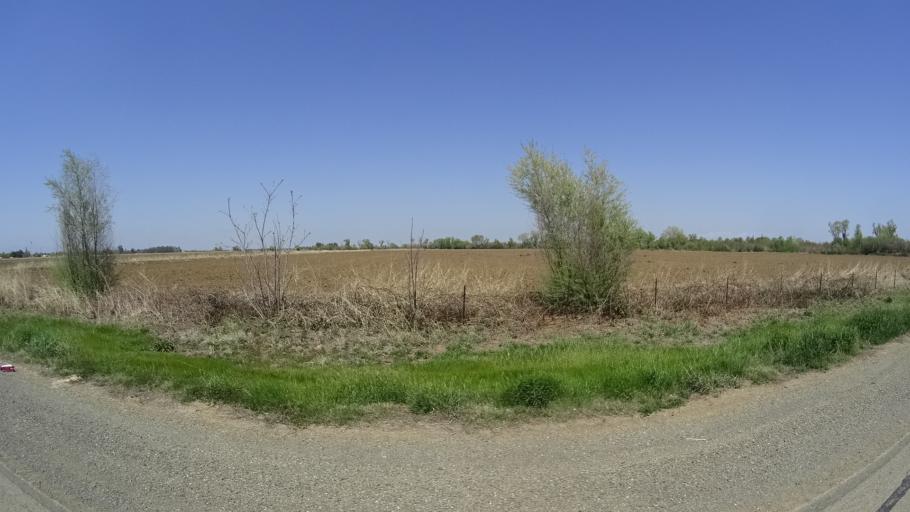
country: US
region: California
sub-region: Glenn County
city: Willows
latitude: 39.5242
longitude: -122.1759
